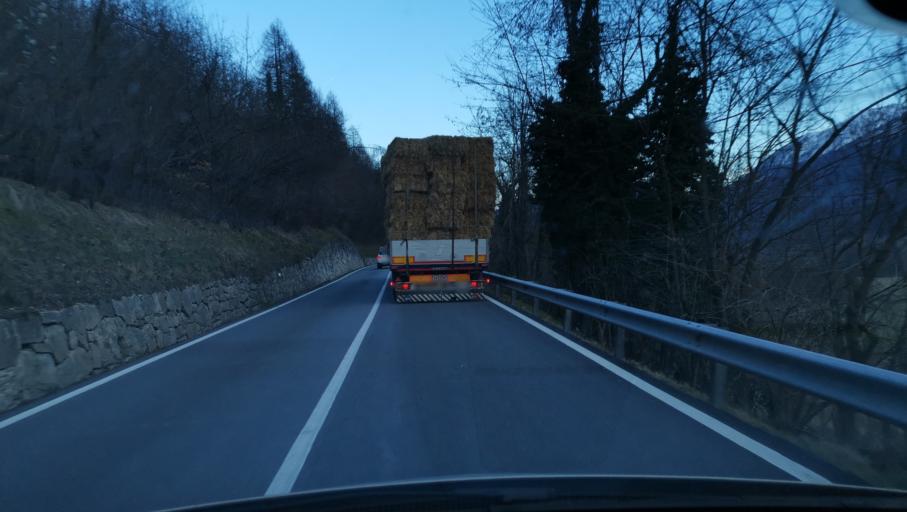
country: IT
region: Piedmont
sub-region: Provincia di Cuneo
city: Demonte
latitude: 44.3138
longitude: 7.2794
